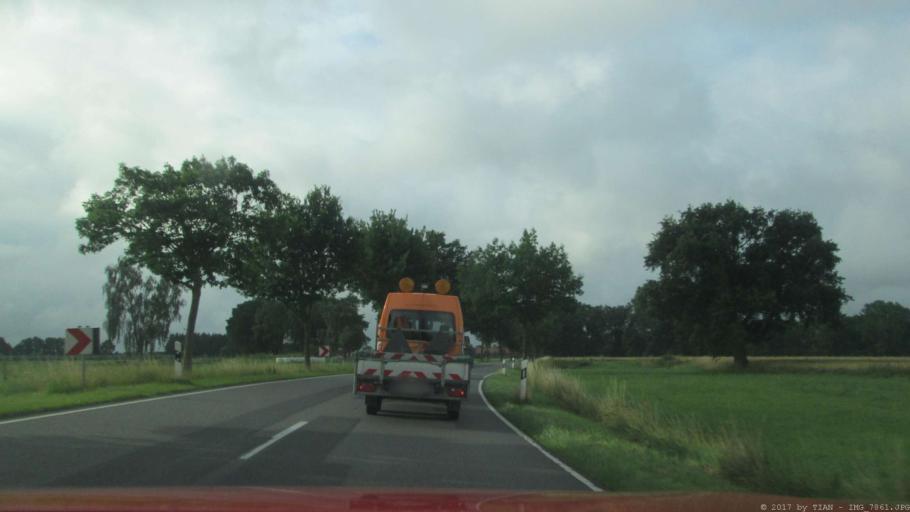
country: DE
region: Lower Saxony
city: Wittingen
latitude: 52.7168
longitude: 10.7639
